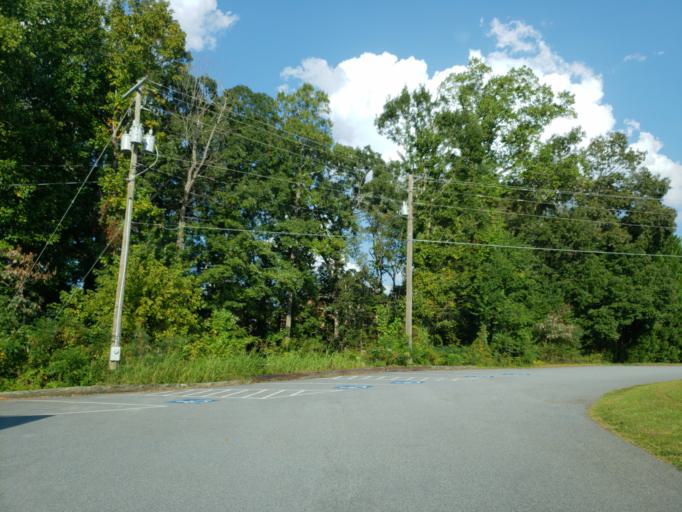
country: US
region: Georgia
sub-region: Fulton County
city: Roswell
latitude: 34.0597
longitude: -84.4353
